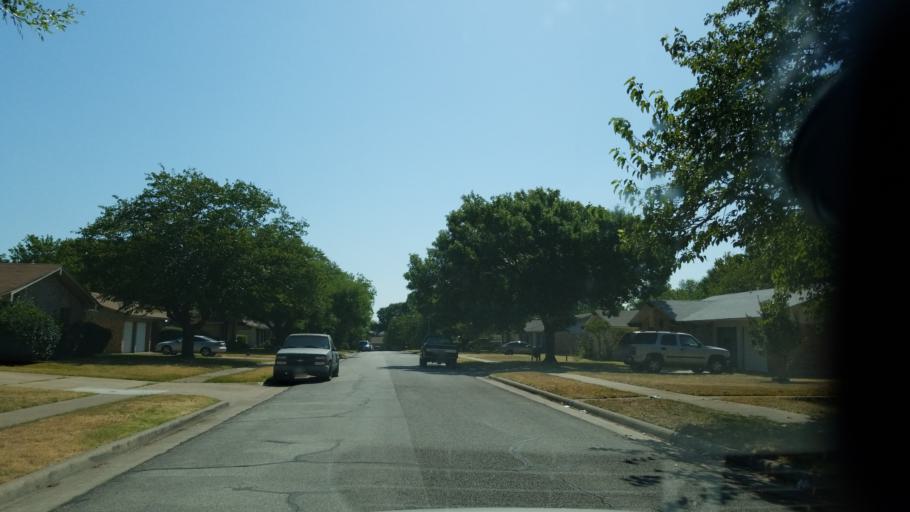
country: US
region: Texas
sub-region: Dallas County
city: Duncanville
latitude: 32.6364
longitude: -96.9028
